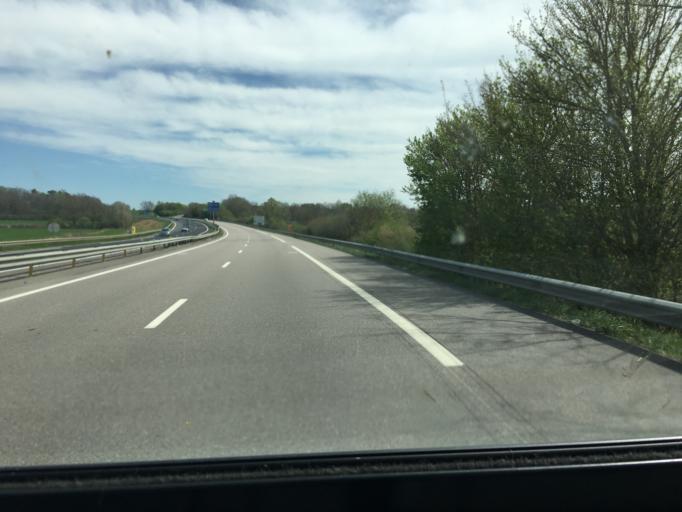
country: FR
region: Lorraine
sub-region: Departement de Meurthe-et-Moselle
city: Ecrouves
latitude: 48.6495
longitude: 5.8588
